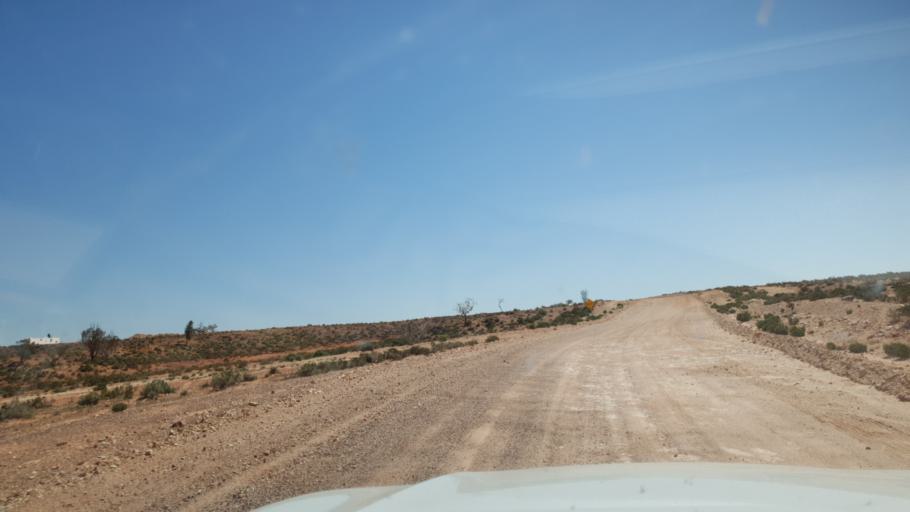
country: AU
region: South Australia
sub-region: Whyalla
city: Whyalla
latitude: -32.6481
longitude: 136.9631
